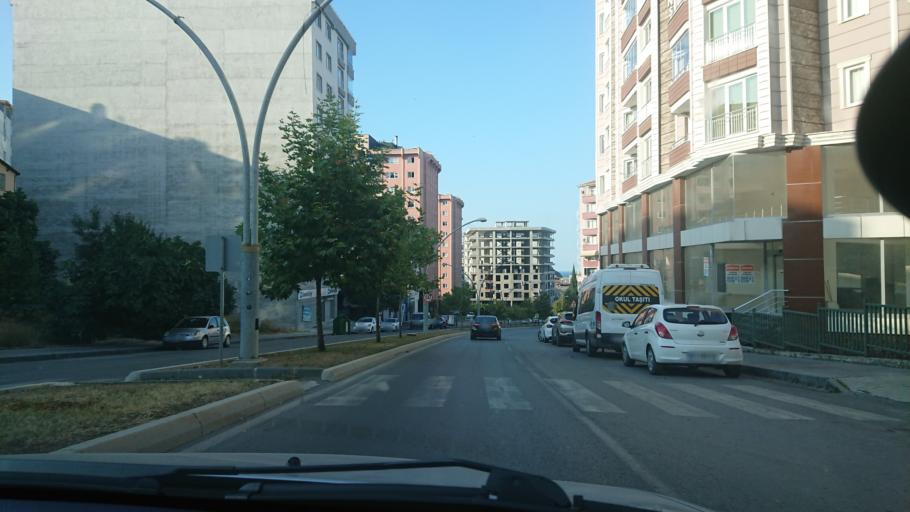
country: TR
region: Samsun
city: Samsun
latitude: 41.2994
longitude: 36.3245
